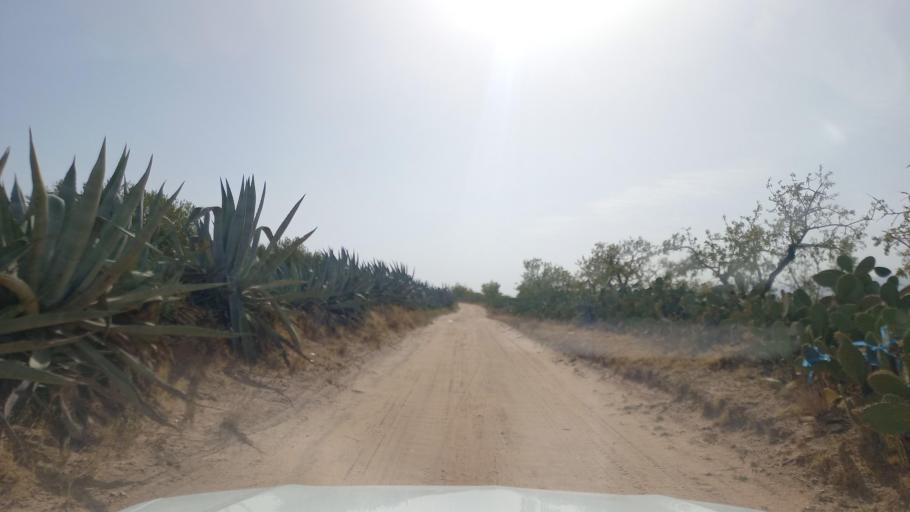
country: TN
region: Al Qasrayn
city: Kasserine
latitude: 35.2072
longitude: 8.9650
